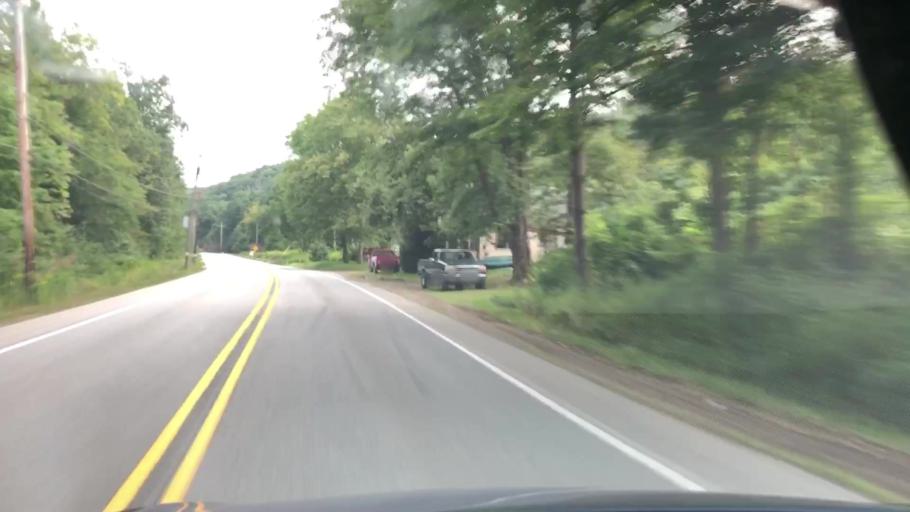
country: US
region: Pennsylvania
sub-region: Venango County
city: Hasson Heights
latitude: 41.4952
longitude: -79.7003
